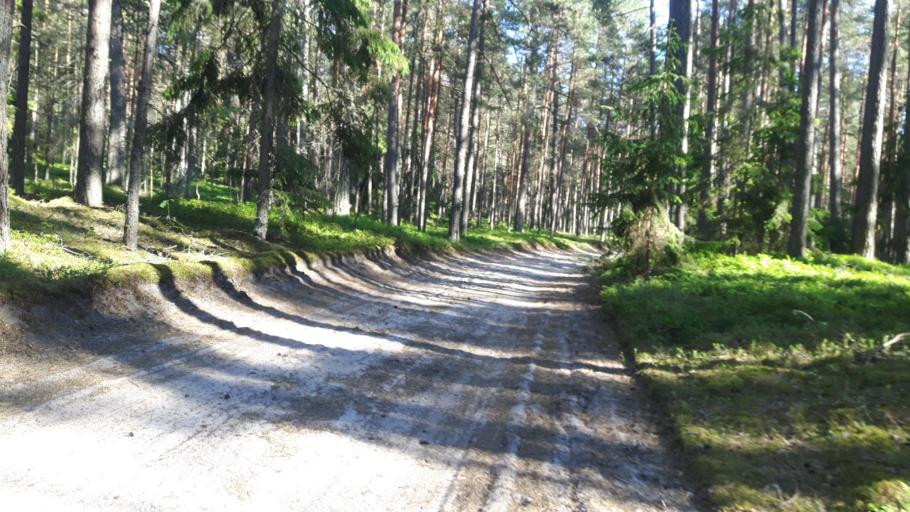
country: LV
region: Salacgrivas
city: Salacgriva
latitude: 57.7125
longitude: 24.3509
